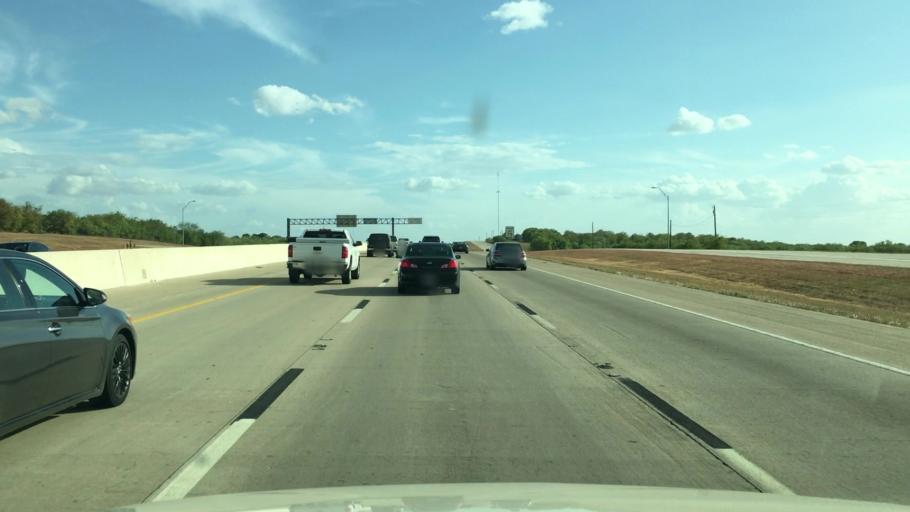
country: US
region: Texas
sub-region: Bell County
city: Salado
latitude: 30.8708
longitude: -97.5829
